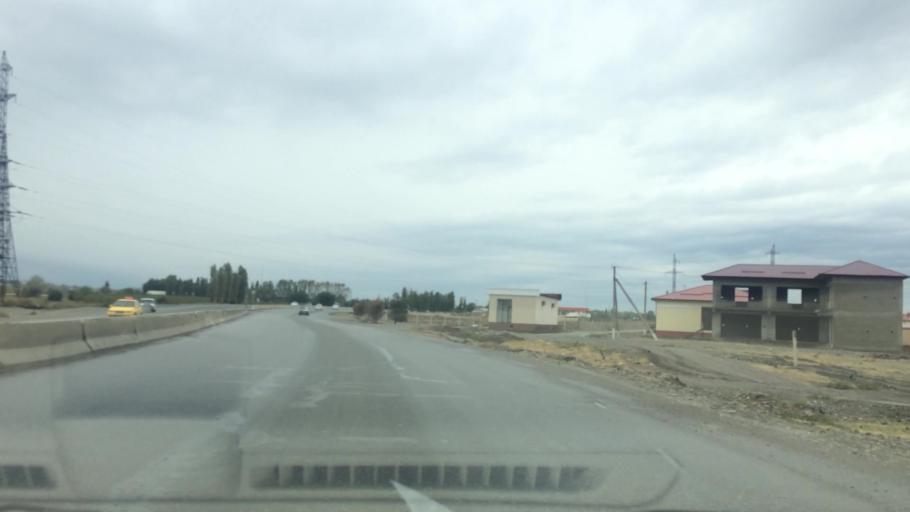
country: UZ
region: Jizzax
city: Jizzax
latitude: 40.0257
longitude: 67.6164
